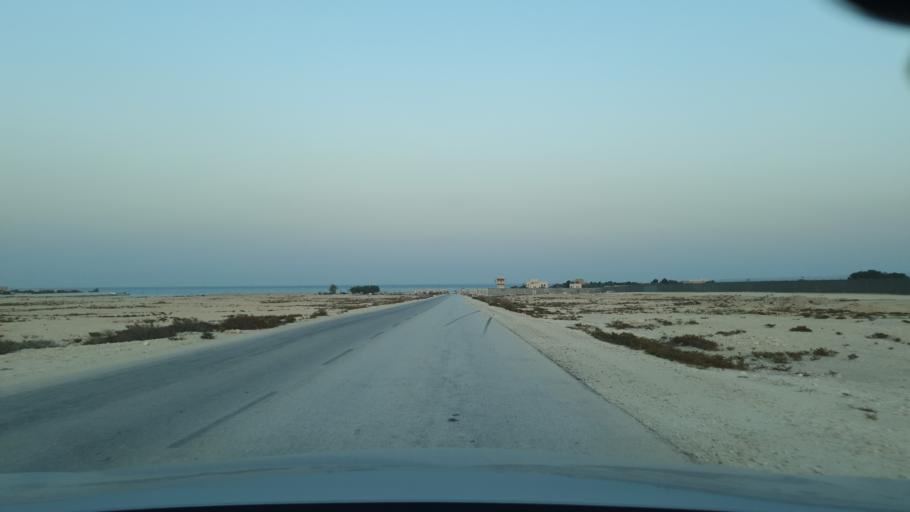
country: BH
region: Central Governorate
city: Dar Kulayb
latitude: 25.9558
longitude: 50.6062
